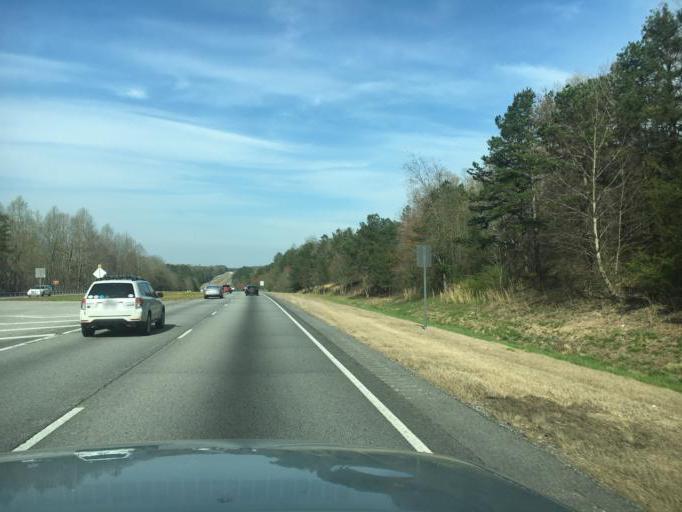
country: US
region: Georgia
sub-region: Hall County
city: Lula
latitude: 34.3968
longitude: -83.6880
